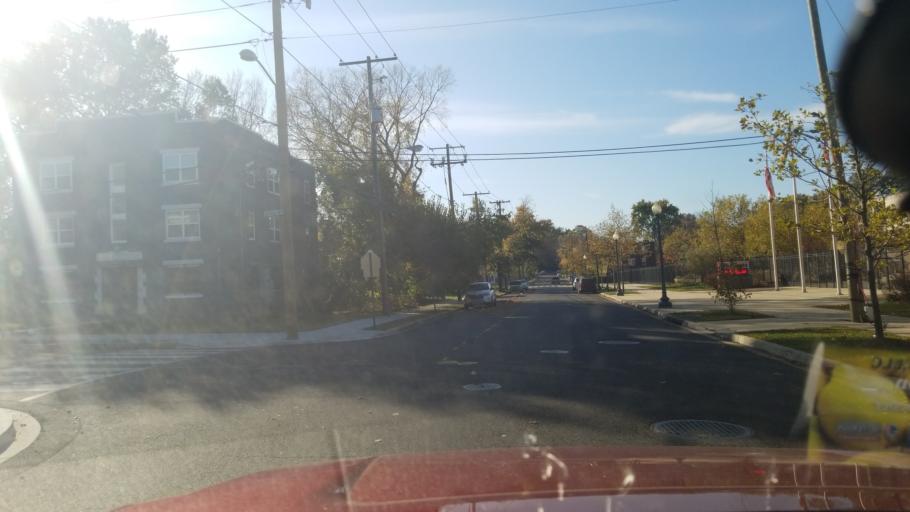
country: US
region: Maryland
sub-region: Prince George's County
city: Fairmount Heights
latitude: 38.8974
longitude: -76.9219
